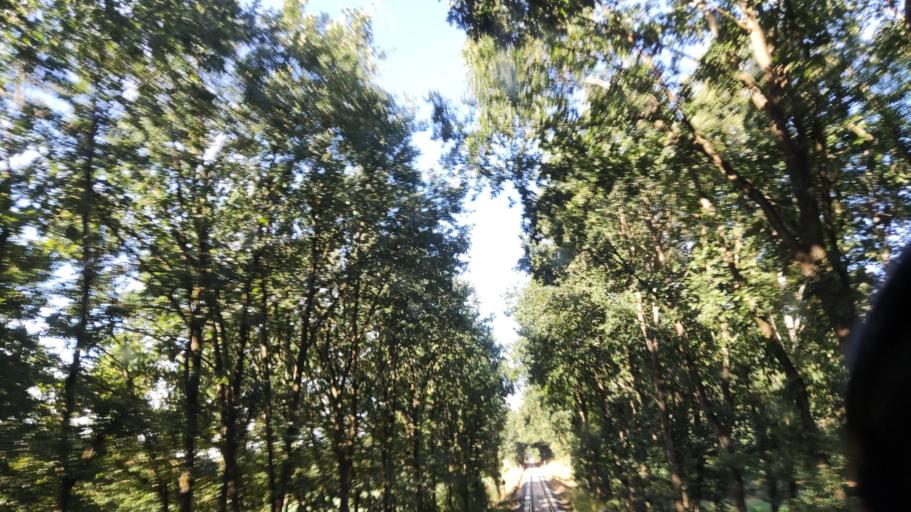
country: DE
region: Lower Saxony
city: Soderstorf
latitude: 53.1122
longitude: 10.0750
